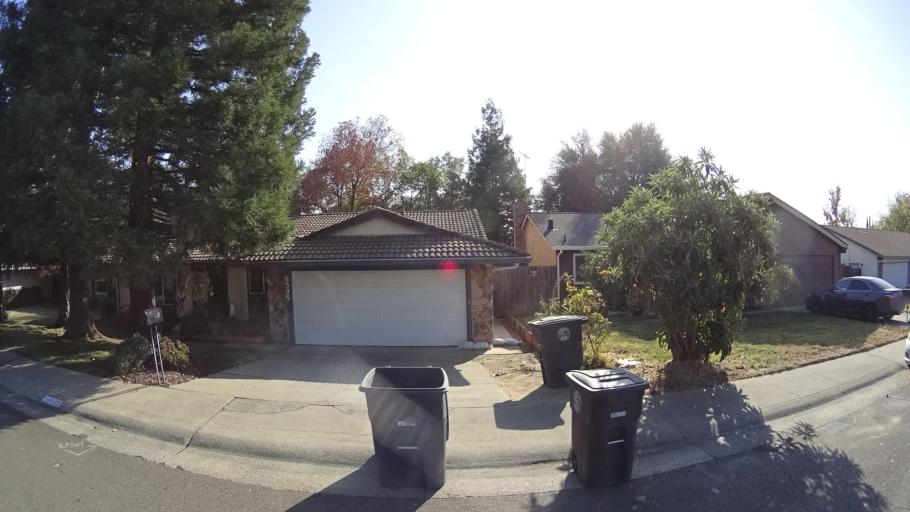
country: US
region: California
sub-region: Sacramento County
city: Citrus Heights
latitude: 38.6879
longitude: -121.2740
